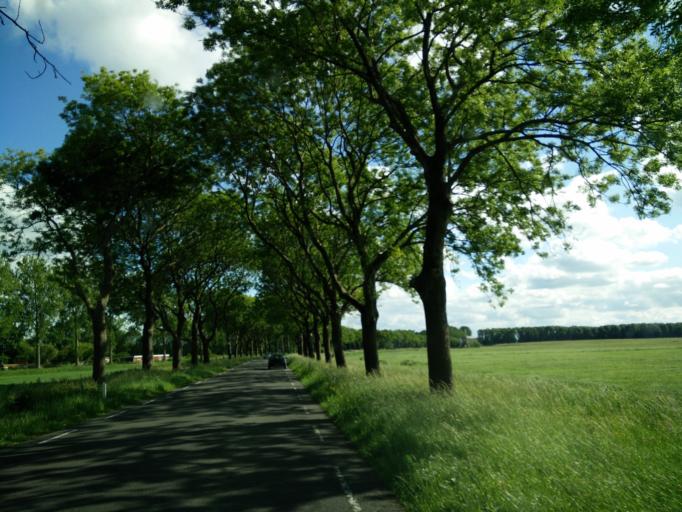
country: NL
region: Groningen
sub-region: Gemeente Groningen
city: Korrewegwijk
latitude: 53.2575
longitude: 6.5870
